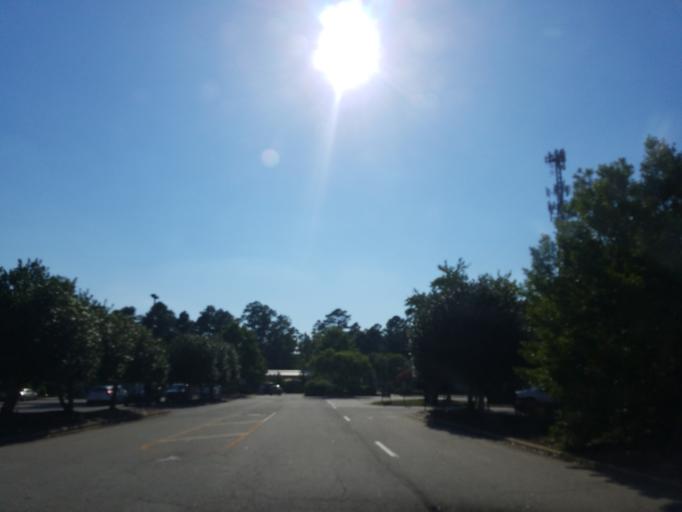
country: US
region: North Carolina
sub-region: Orange County
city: Chapel Hill
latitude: 35.8994
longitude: -79.0131
